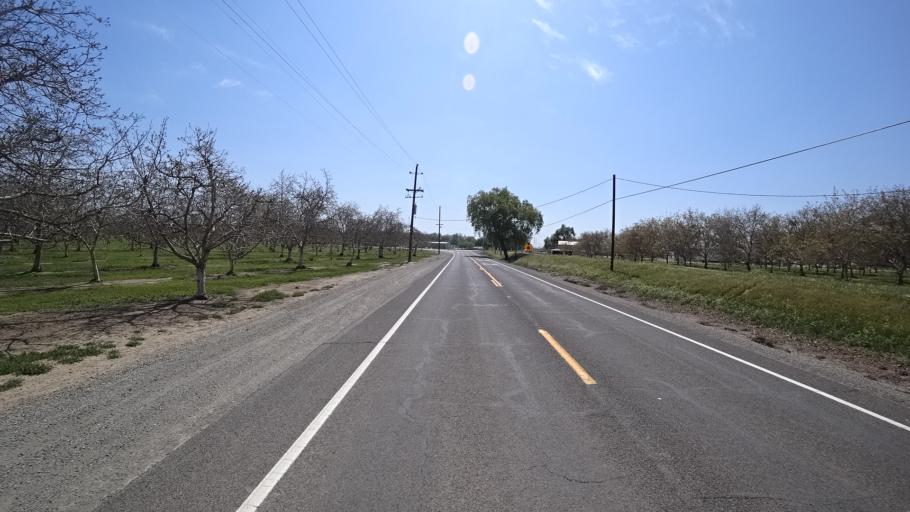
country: US
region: California
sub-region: Glenn County
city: Willows
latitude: 39.4592
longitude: -122.0178
